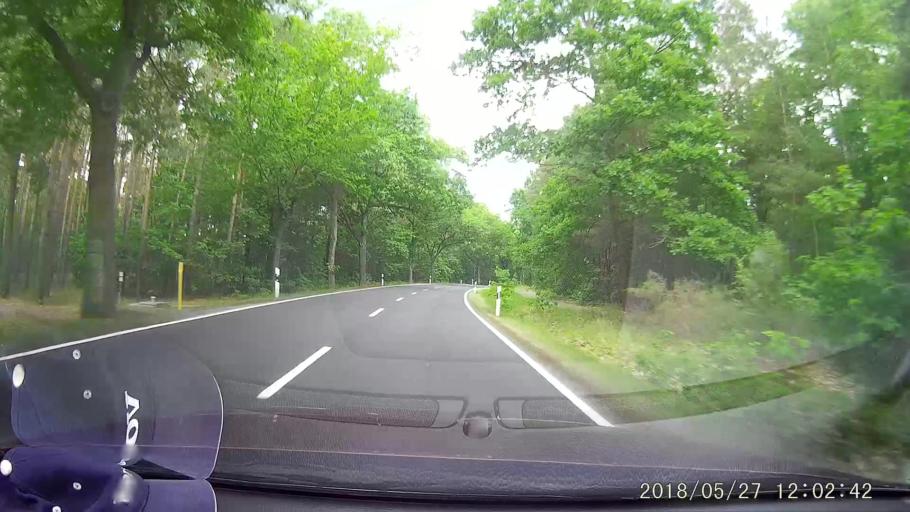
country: DE
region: Saxony
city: Mucka
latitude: 51.3376
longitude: 14.6869
